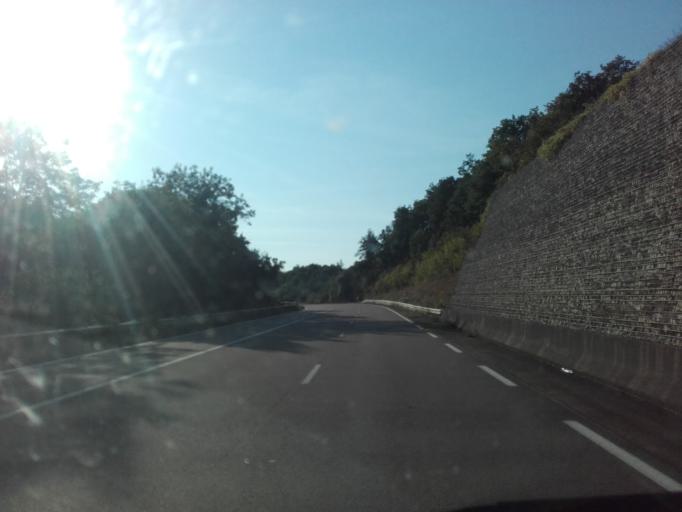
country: FR
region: Bourgogne
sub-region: Departement de l'Yonne
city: Venoy
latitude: 47.8124
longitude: 3.7084
